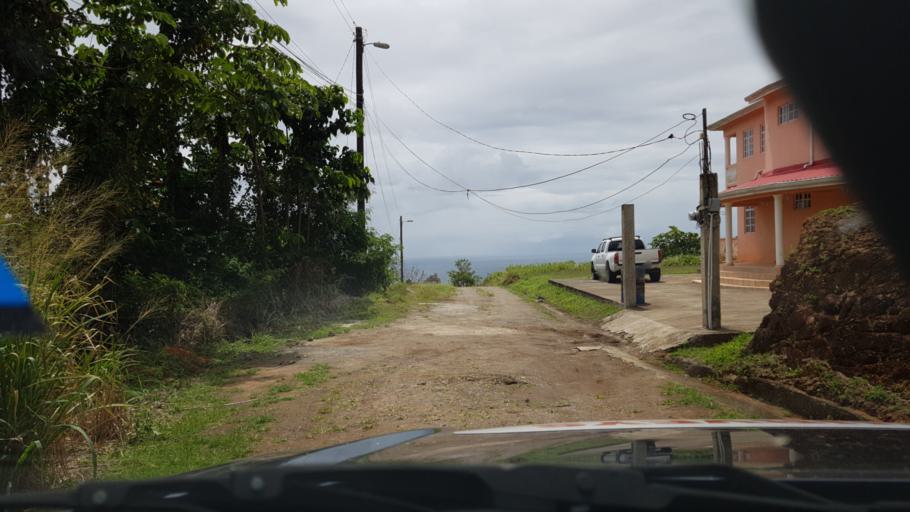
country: LC
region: Anse-la-Raye
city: Anse La Raye
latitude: 13.9443
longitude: -61.0316
